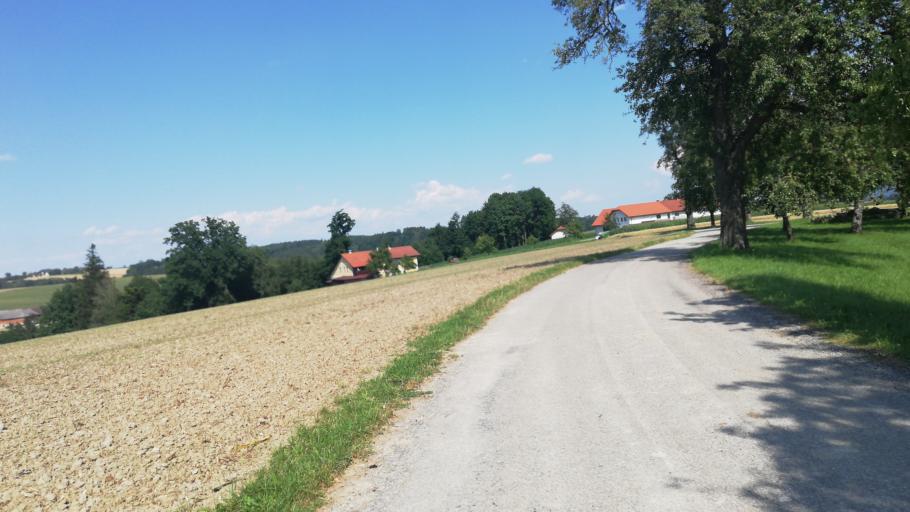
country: AT
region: Upper Austria
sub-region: Wels-Land
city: Edt bei Lambach
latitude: 48.1604
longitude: 13.9010
